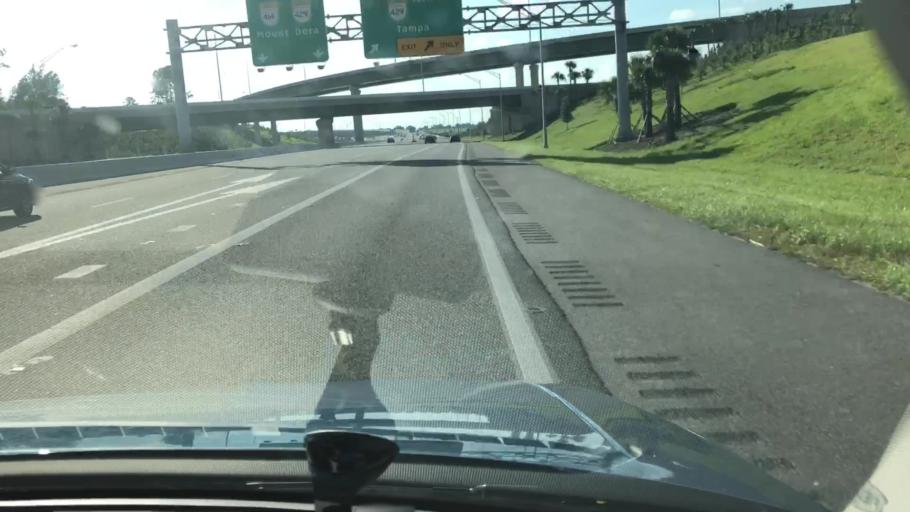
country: US
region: Florida
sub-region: Orange County
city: South Apopka
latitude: 28.6531
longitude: -81.5287
